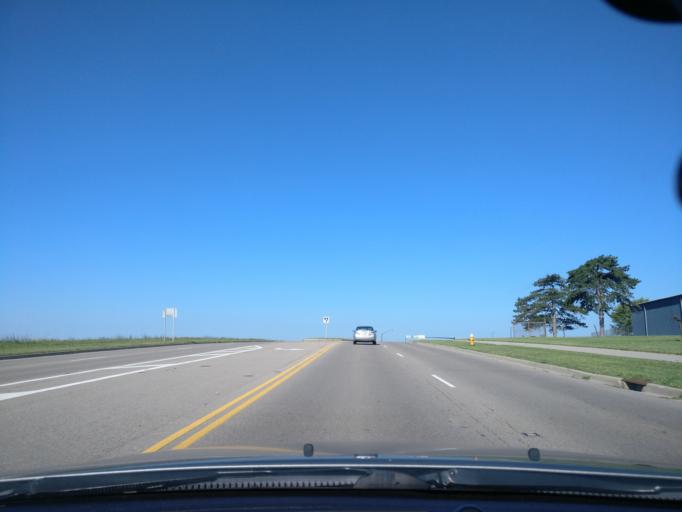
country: US
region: Ohio
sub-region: Warren County
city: Five Points
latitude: 39.5969
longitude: -84.2234
